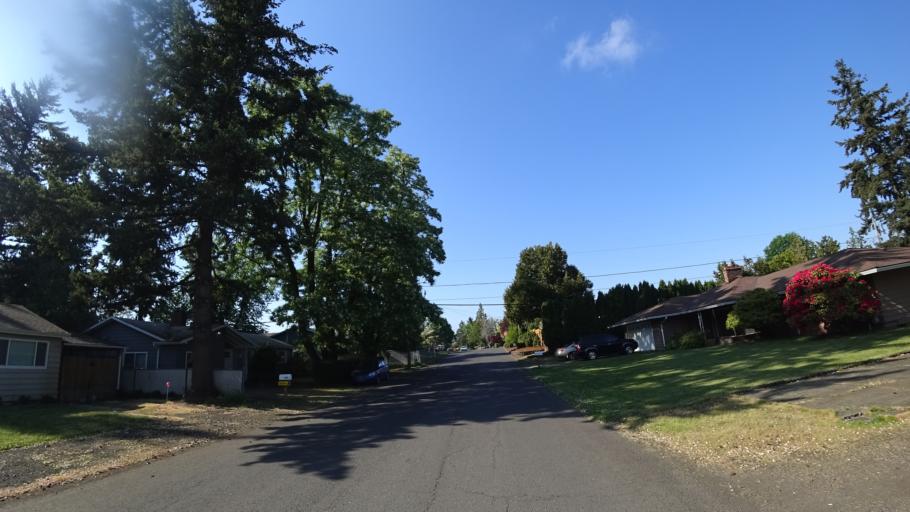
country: US
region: Oregon
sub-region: Clackamas County
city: Happy Valley
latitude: 45.5080
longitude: -122.5004
